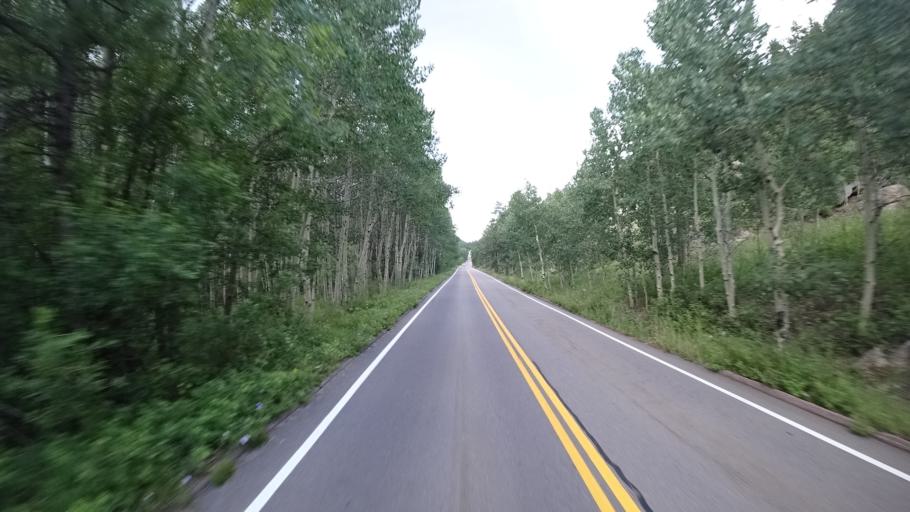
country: US
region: Colorado
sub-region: El Paso County
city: Cascade-Chipita Park
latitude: 38.9026
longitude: -105.0051
